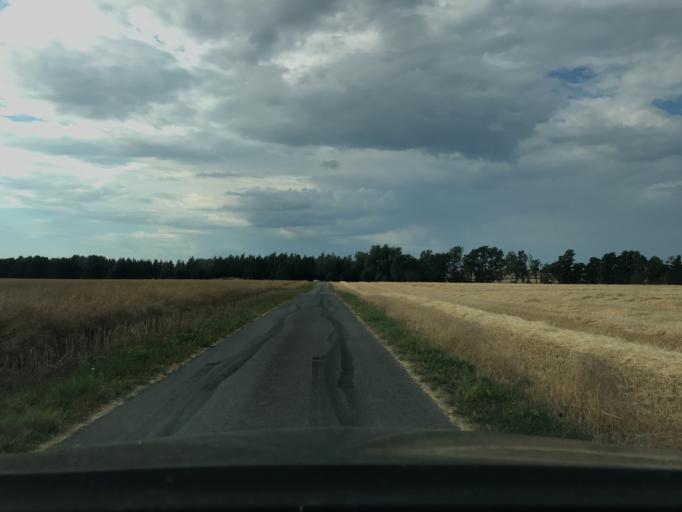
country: SE
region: Skane
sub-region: Simrishamns Kommun
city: Kivik
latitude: 55.5388
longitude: 14.1537
